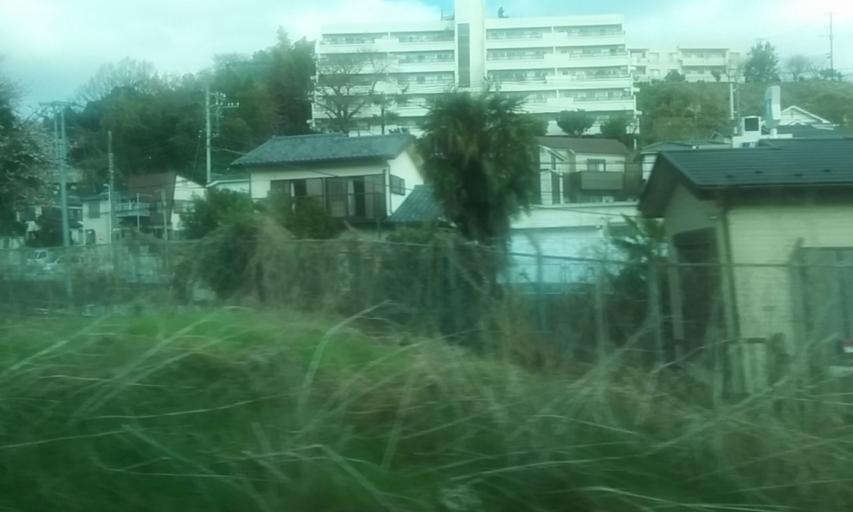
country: JP
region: Kanagawa
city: Yokohama
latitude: 35.4431
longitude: 139.5695
